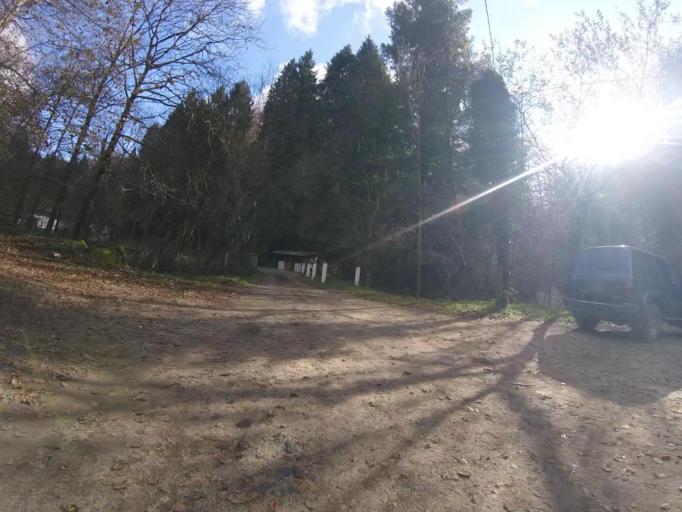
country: ES
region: Navarre
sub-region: Provincia de Navarra
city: Arantza
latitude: 43.2125
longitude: -1.7987
